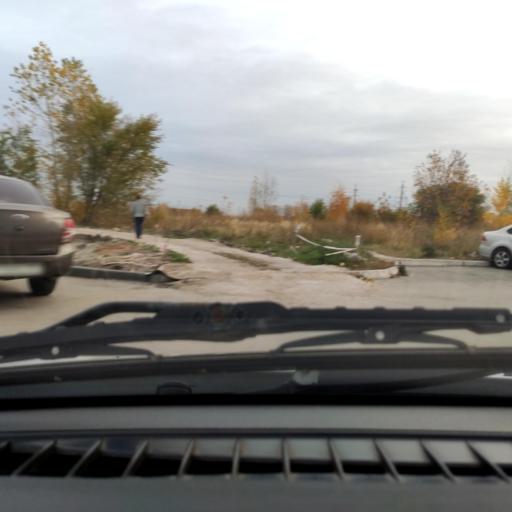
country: RU
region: Samara
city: Tol'yatti
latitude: 53.5419
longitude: 49.3984
